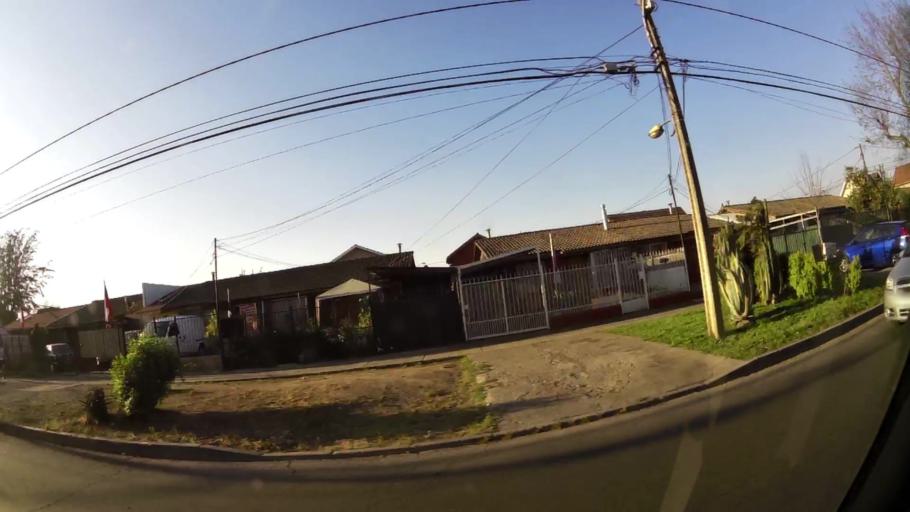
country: CL
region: Santiago Metropolitan
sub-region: Provincia de Santiago
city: Lo Prado
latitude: -33.4750
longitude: -70.7449
